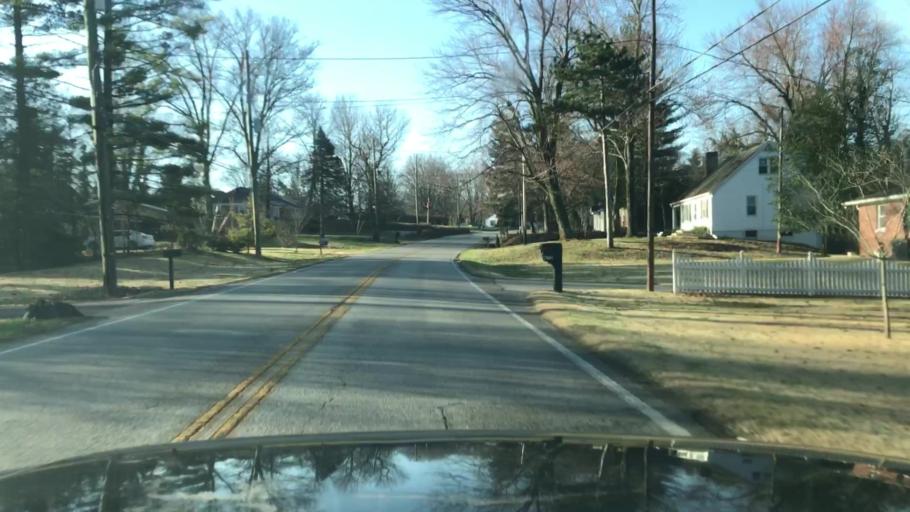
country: US
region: Indiana
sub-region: Vanderburgh County
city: Highland
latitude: 38.0402
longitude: -87.5621
